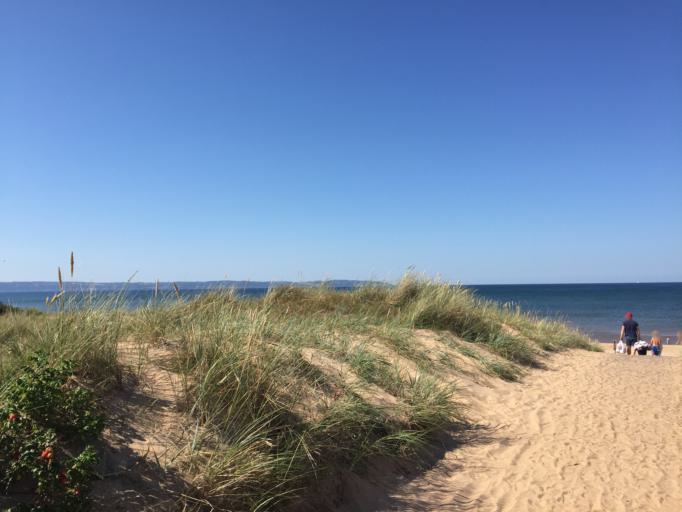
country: SE
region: Halland
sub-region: Laholms Kommun
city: Mellbystrand
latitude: 56.5083
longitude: 12.9419
